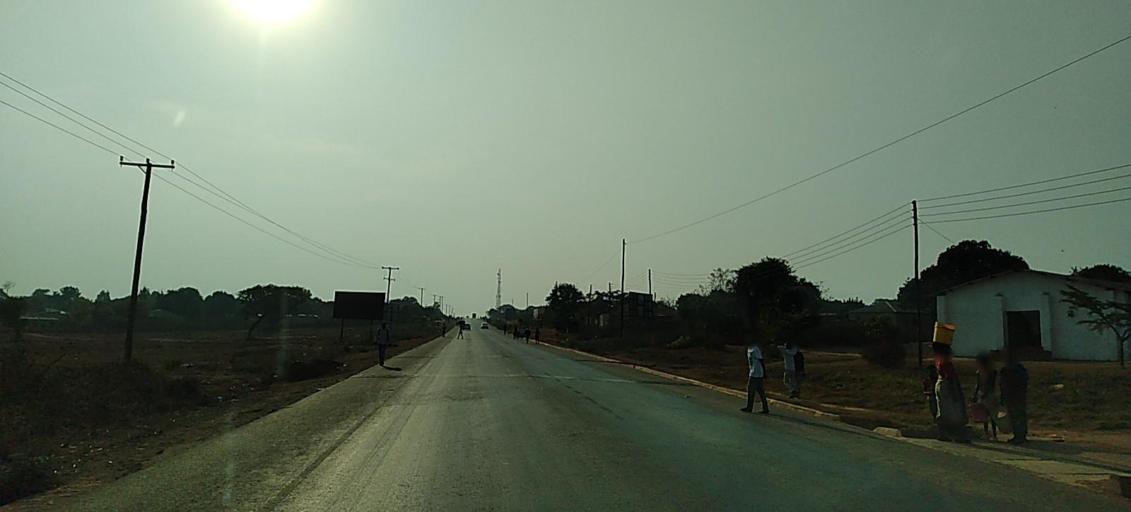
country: ZM
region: North-Western
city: Solwezi
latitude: -12.1902
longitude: 26.4366
